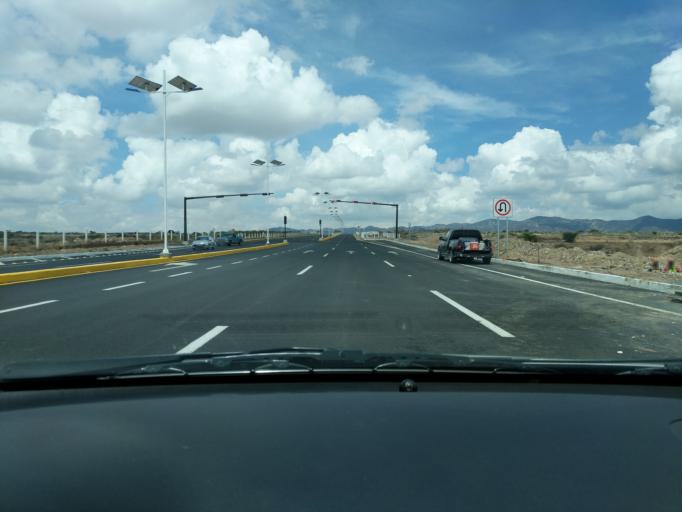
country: MX
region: San Luis Potosi
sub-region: Mexquitic de Carmona
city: Guadalupe Victoria
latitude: 22.1660
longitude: -101.0520
